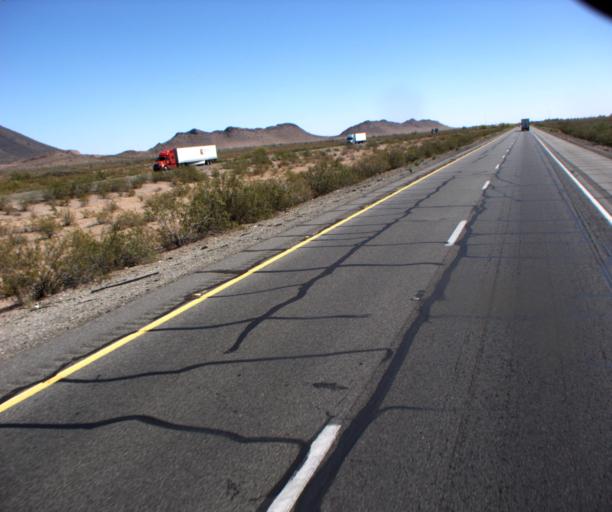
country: US
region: Arizona
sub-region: Maricopa County
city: Buckeye
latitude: 33.5238
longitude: -113.0904
